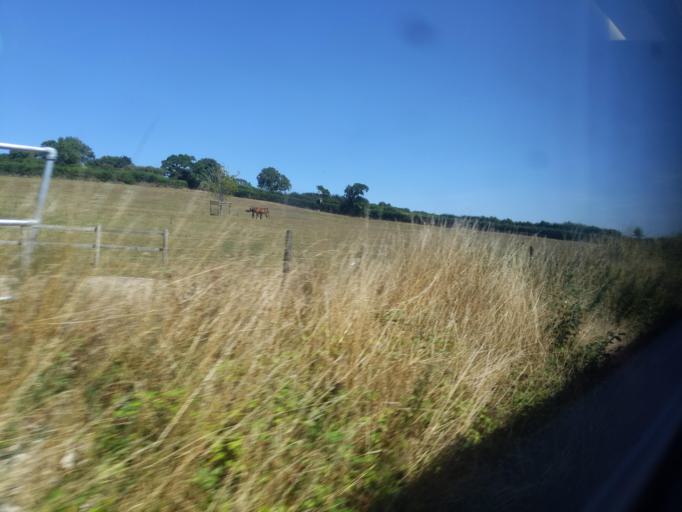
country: GB
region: England
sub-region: Devon
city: Ivybridge
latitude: 50.3946
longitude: -3.9356
